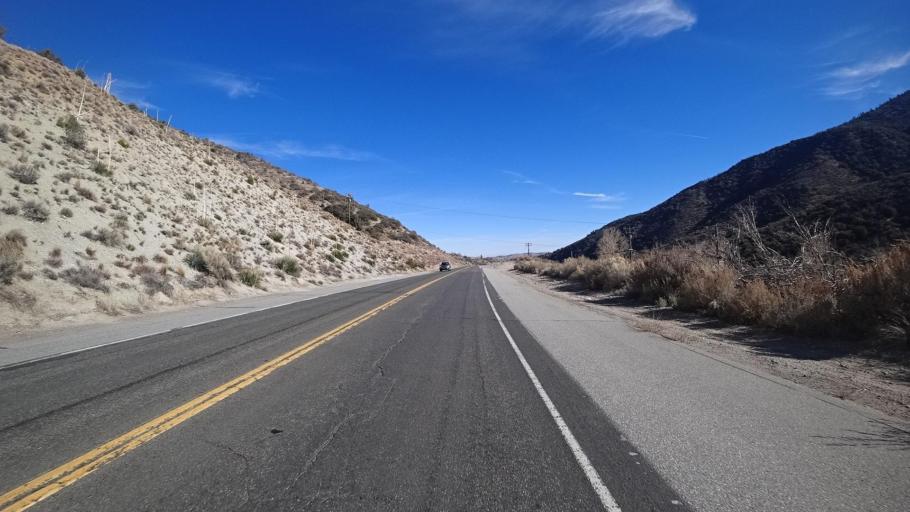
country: US
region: California
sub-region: Kern County
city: Frazier Park
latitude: 34.8202
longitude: -118.9721
